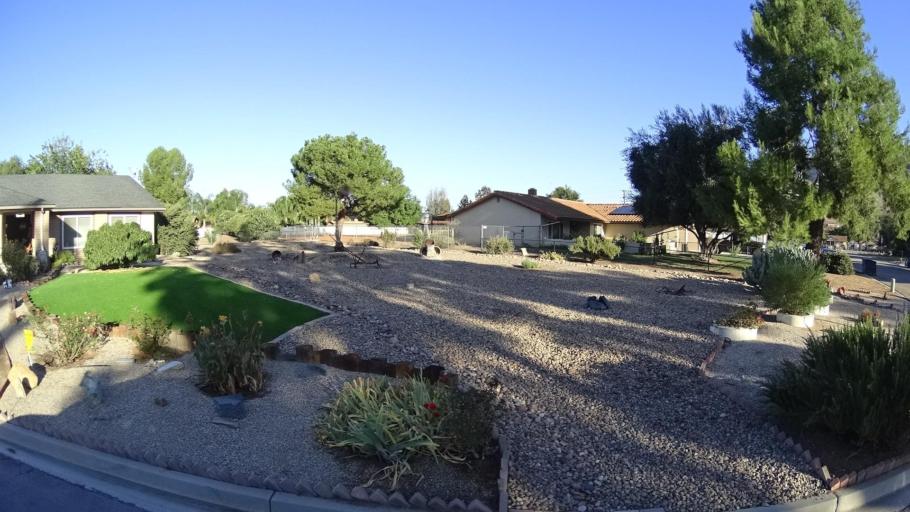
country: US
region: California
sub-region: San Diego County
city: Lakeside
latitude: 32.8752
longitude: -116.9172
